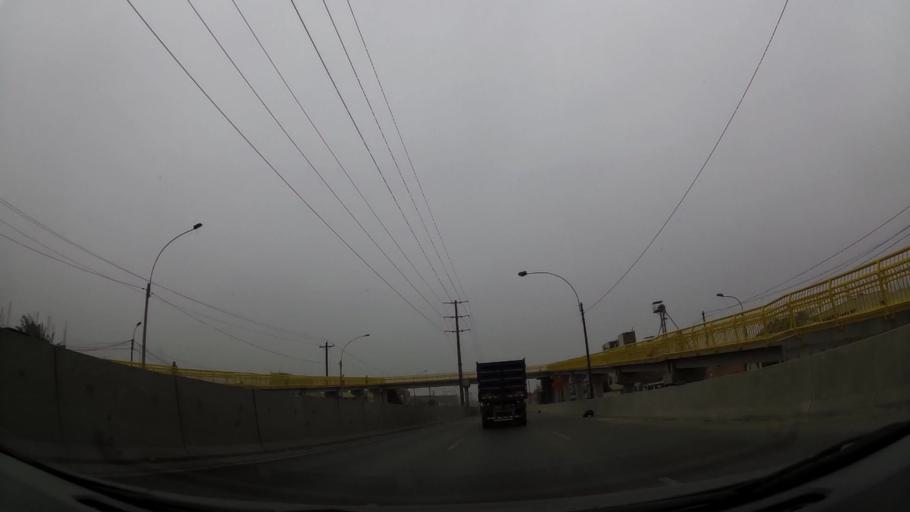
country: PE
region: Lima
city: Ventanilla
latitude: -11.8593
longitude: -77.0815
